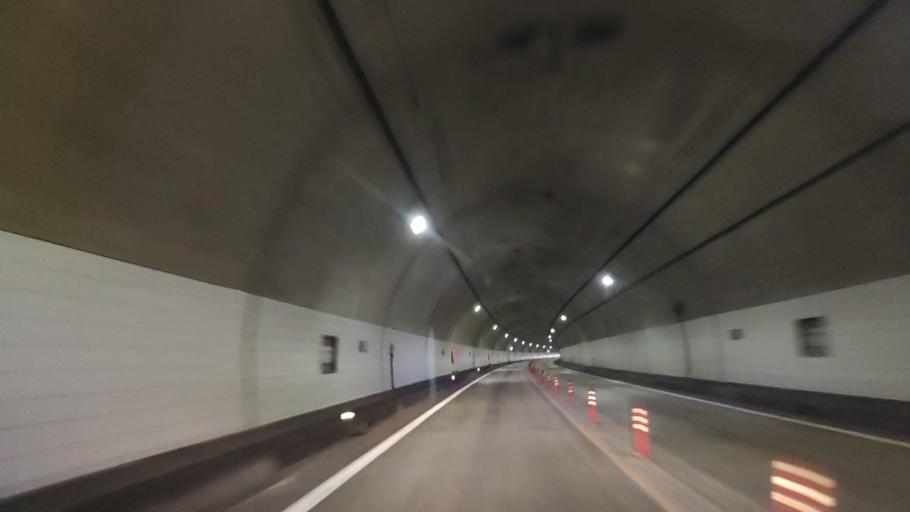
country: JP
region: Akita
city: Odate
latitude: 40.3615
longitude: 140.6950
